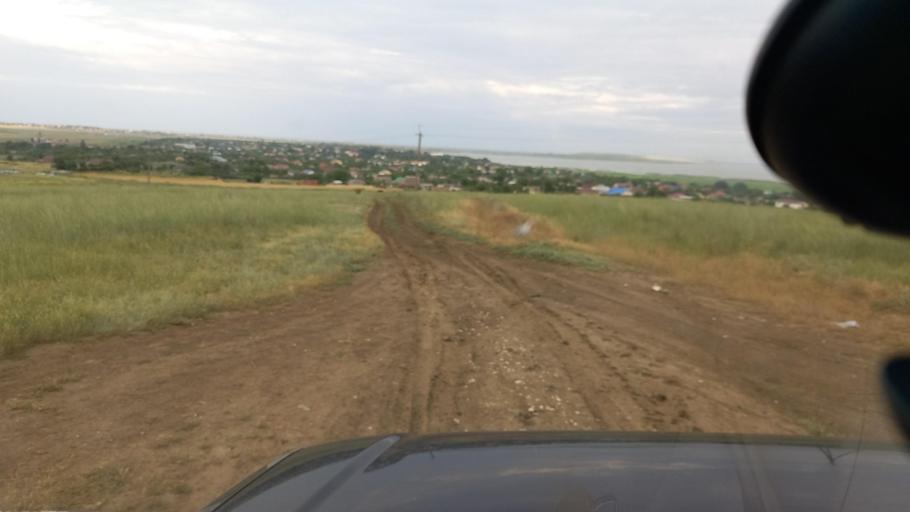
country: RU
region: Krasnodarskiy
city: Akhtanizovskaya
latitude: 45.3127
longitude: 37.0834
